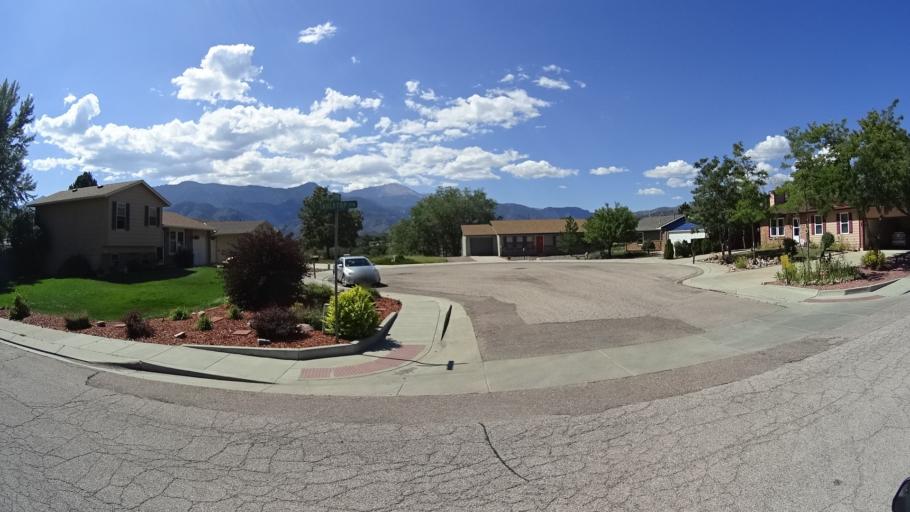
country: US
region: Colorado
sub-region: El Paso County
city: Colorado Springs
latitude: 38.8545
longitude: -104.8535
